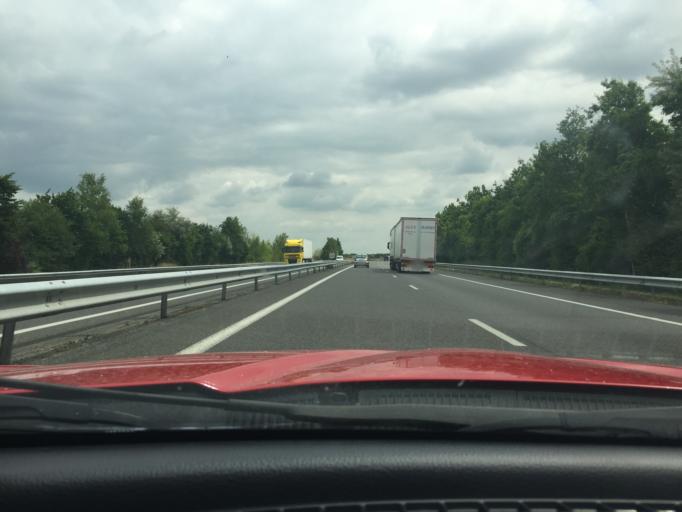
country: FR
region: Picardie
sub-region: Departement de l'Aisne
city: Liesse-Notre-Dame
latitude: 49.5626
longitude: 3.7890
